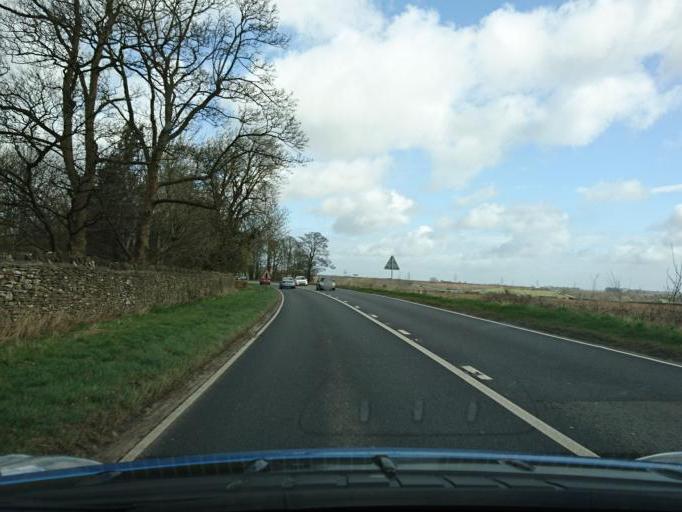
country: GB
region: England
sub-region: South Gloucestershire
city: Cold Ashton
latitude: 51.4767
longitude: -2.3624
